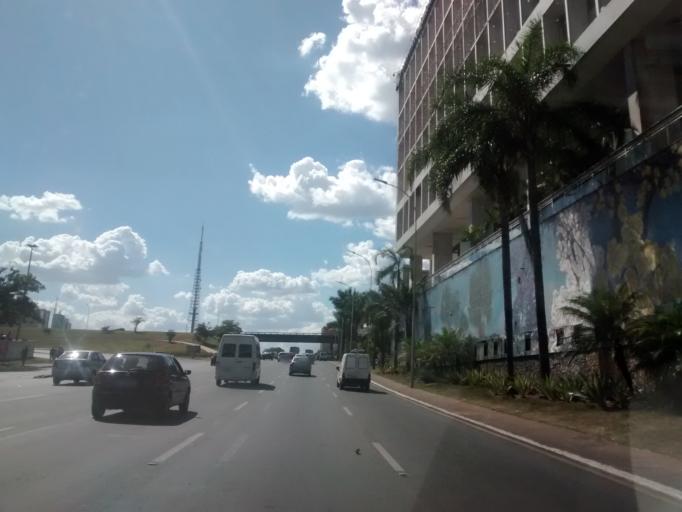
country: BR
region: Federal District
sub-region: Brasilia
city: Brasilia
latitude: -15.7924
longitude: -47.8835
